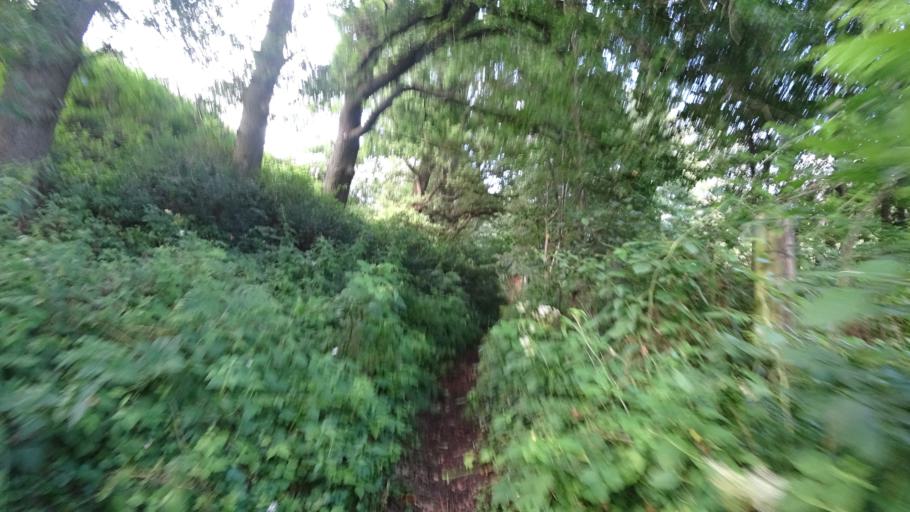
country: DE
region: North Rhine-Westphalia
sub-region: Regierungsbezirk Detmold
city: Steinhagen
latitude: 51.9447
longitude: 8.4465
